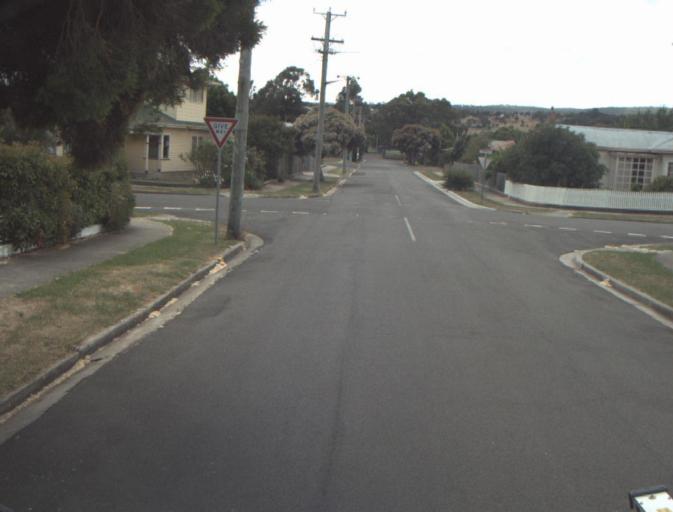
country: AU
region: Tasmania
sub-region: Launceston
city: Newstead
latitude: -41.4383
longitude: 147.1635
